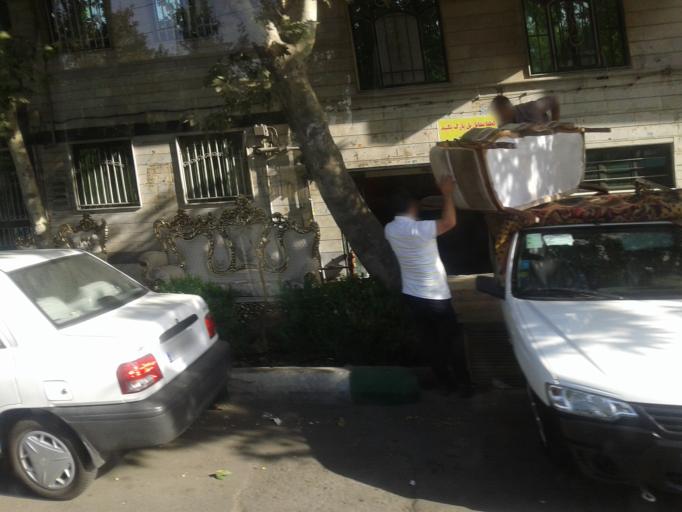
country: IR
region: Tehran
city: Tehran
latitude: 35.6535
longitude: 51.3157
